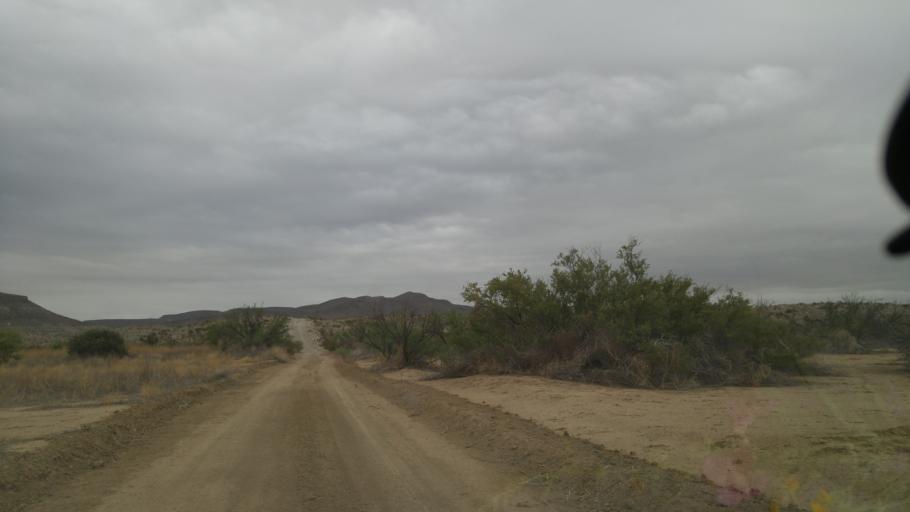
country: US
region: Texas
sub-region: Brewster County
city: Alpine
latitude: 29.5791
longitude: -103.3629
